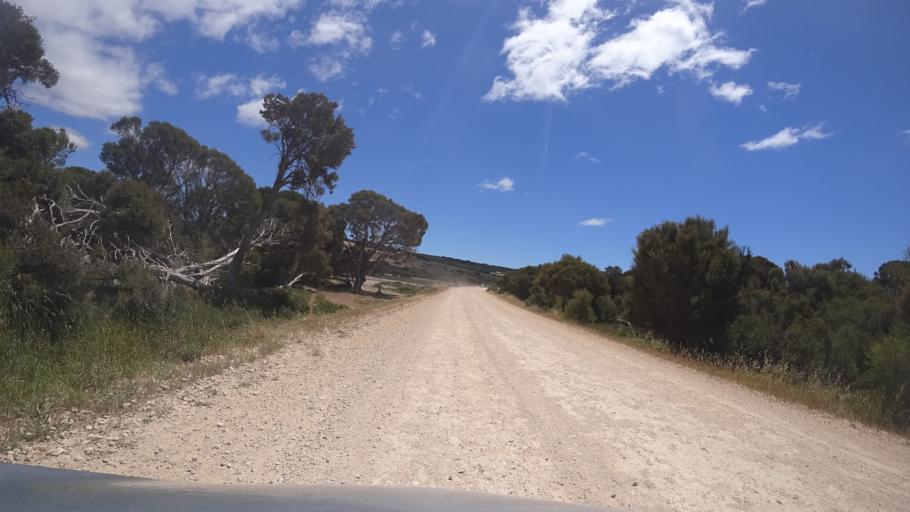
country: AU
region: South Australia
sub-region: Yankalilla
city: Normanville
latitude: -35.8009
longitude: 138.0657
